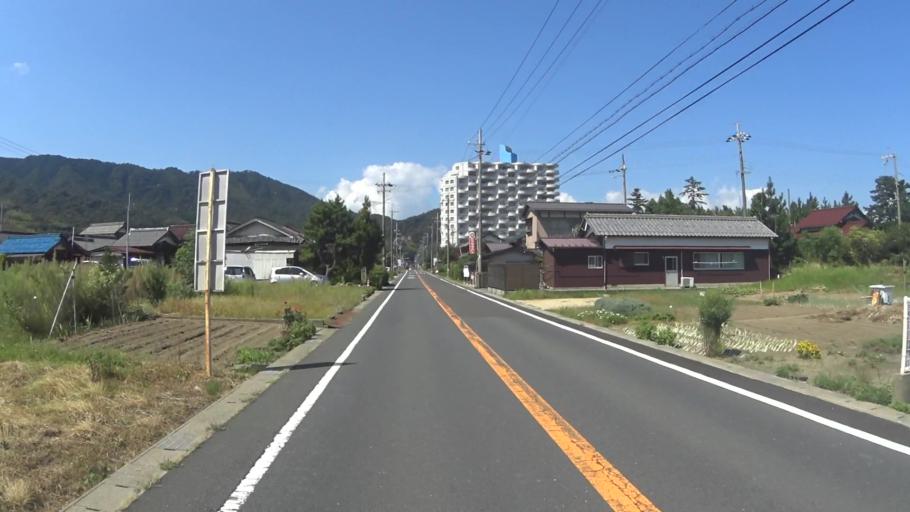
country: JP
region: Kyoto
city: Maizuru
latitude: 35.5190
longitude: 135.2816
